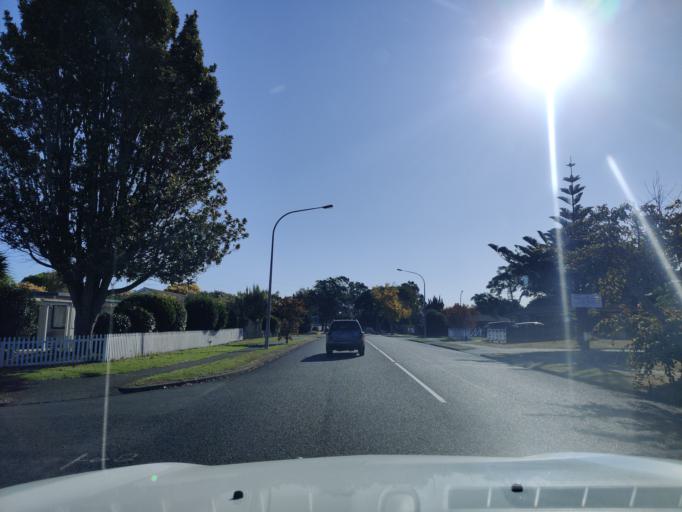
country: NZ
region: Auckland
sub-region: Auckland
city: Takanini
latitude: -37.0438
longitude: 174.9165
